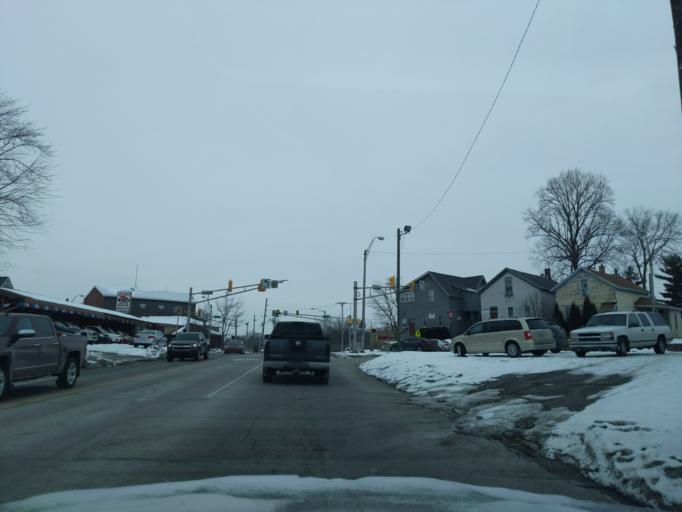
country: US
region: Indiana
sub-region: Tippecanoe County
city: Lafayette
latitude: 40.4155
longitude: -86.8772
